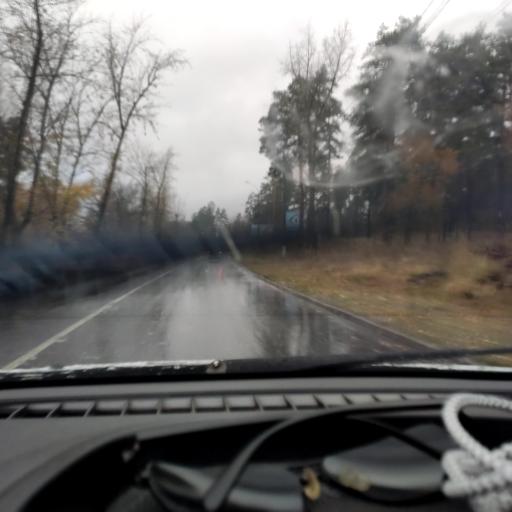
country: RU
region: Samara
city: Tol'yatti
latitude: 53.4738
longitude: 49.3795
